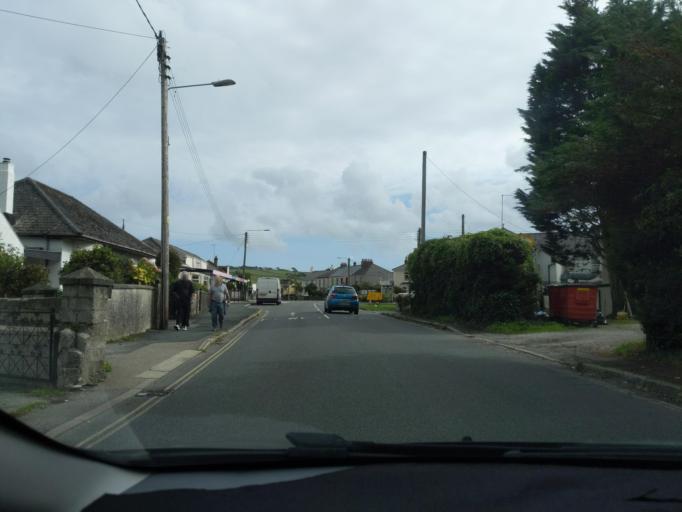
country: GB
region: England
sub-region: Cornwall
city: Par
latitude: 50.3522
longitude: -4.7000
